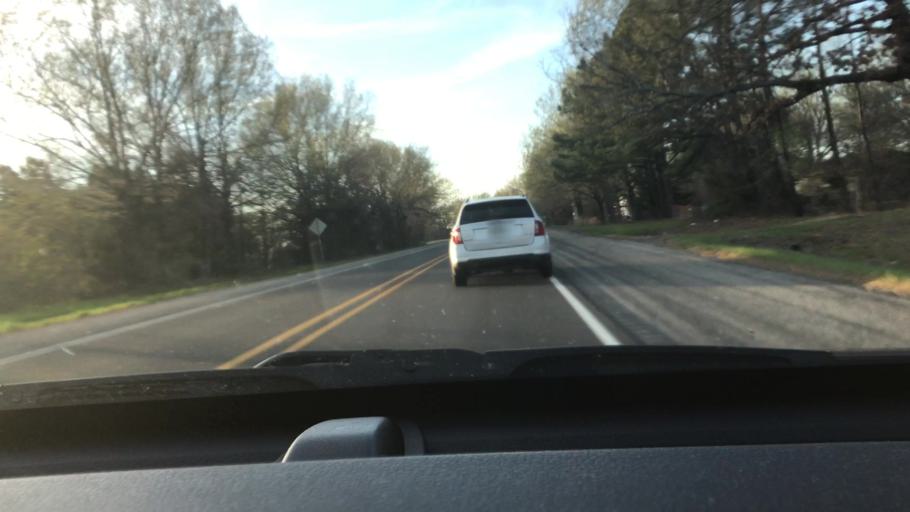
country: US
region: Texas
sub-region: Red River County
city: Clarksville
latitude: 33.5876
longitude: -94.9404
